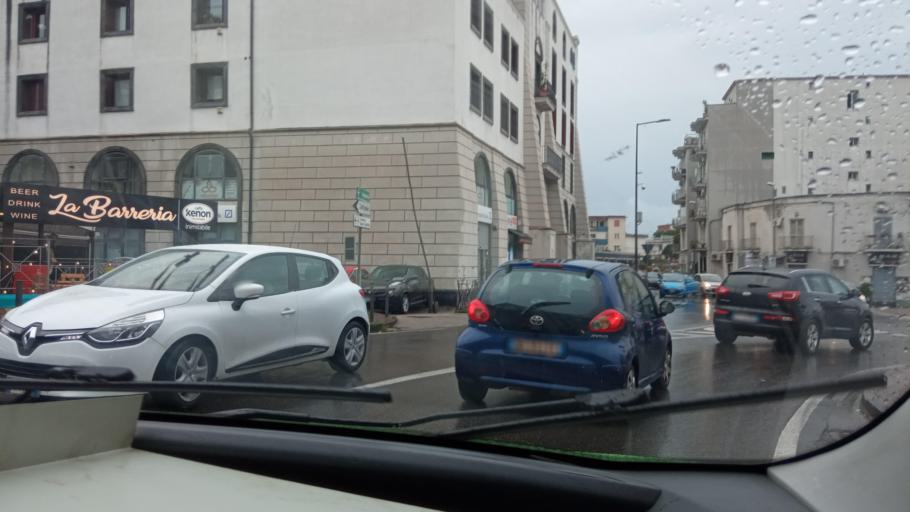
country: IT
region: Campania
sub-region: Provincia di Napoli
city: Pozzuoli
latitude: 40.8308
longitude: 14.1199
